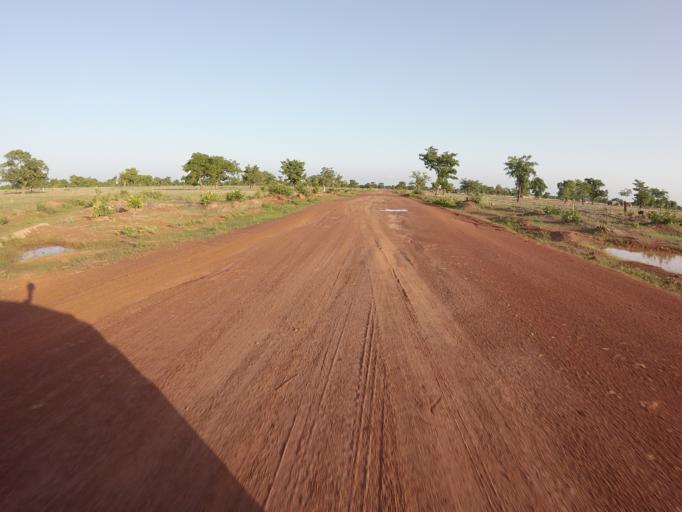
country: TG
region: Savanes
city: Sansanne-Mango
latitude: 10.2933
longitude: -0.0877
